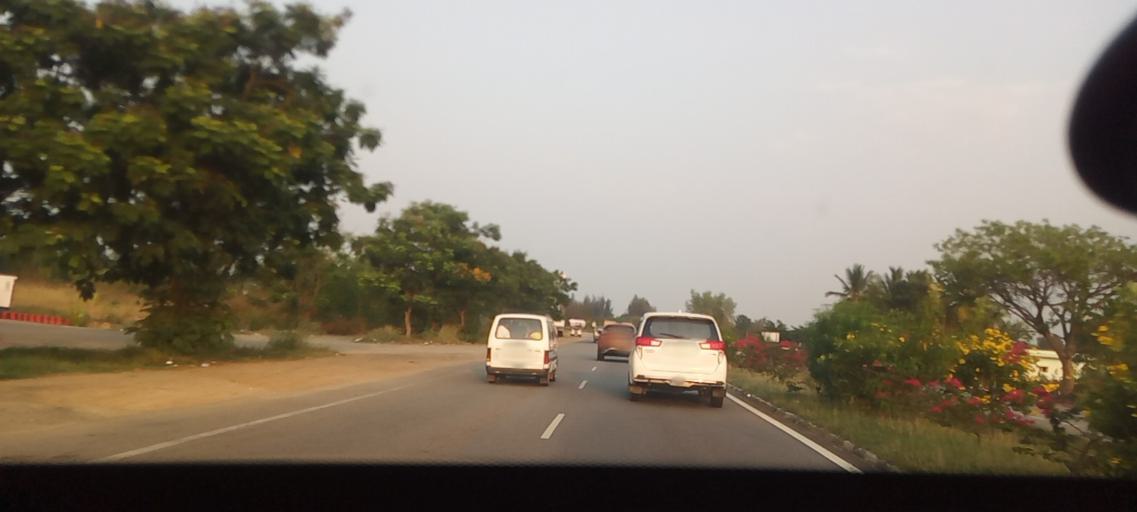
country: IN
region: Karnataka
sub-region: Tumkur
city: Kunigal
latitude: 12.9970
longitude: 76.9244
